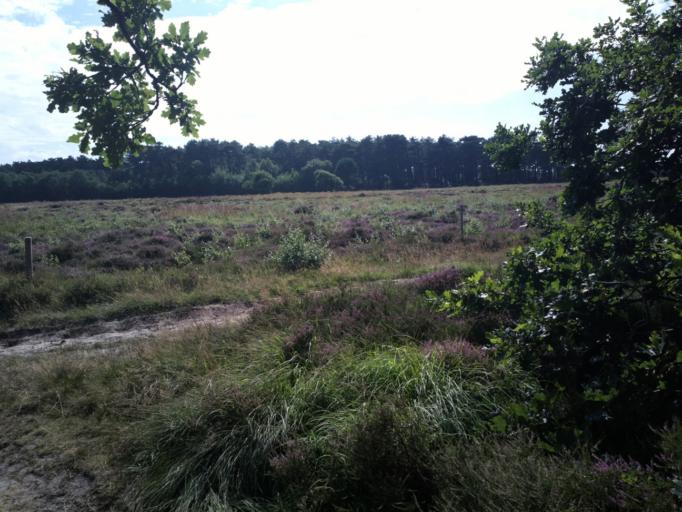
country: NL
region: North Holland
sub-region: Gemeente Texel
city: Den Burg
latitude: 53.0748
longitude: 4.7530
